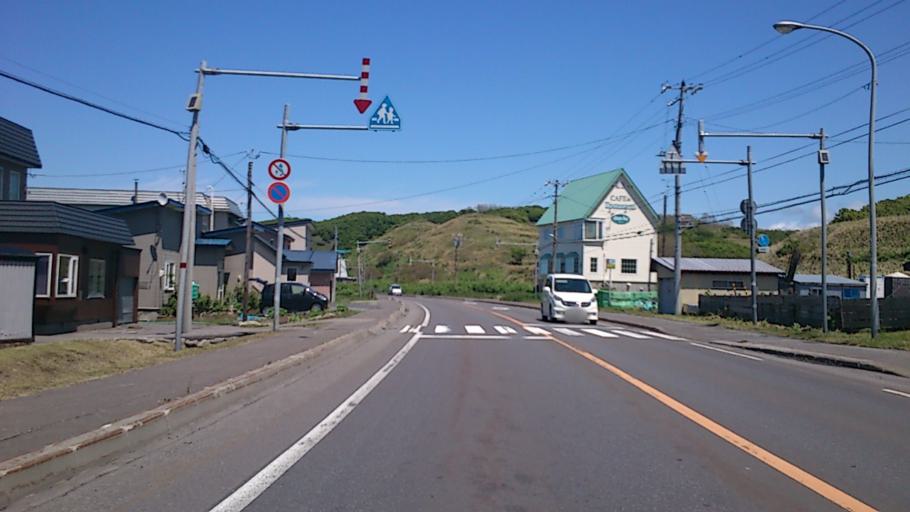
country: JP
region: Hokkaido
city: Rumoi
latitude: 43.9650
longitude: 141.6451
